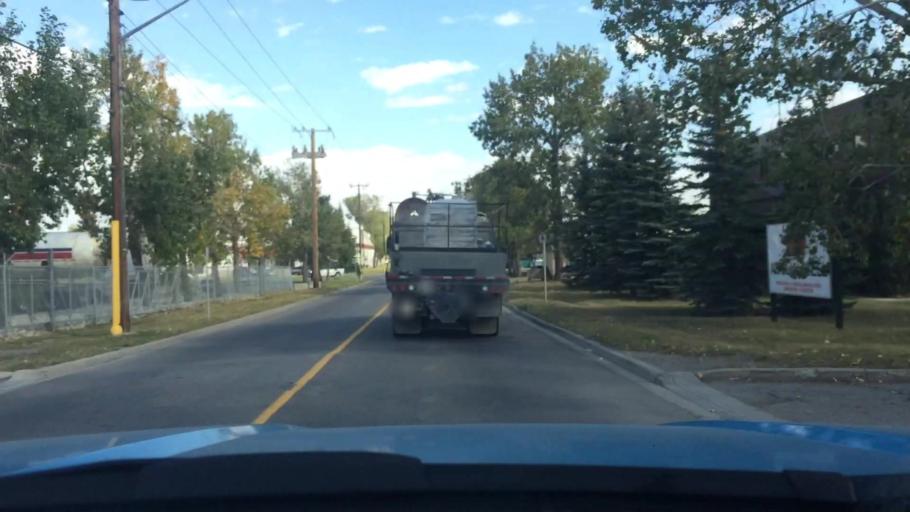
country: CA
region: Alberta
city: Calgary
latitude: 50.9978
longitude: -113.9765
